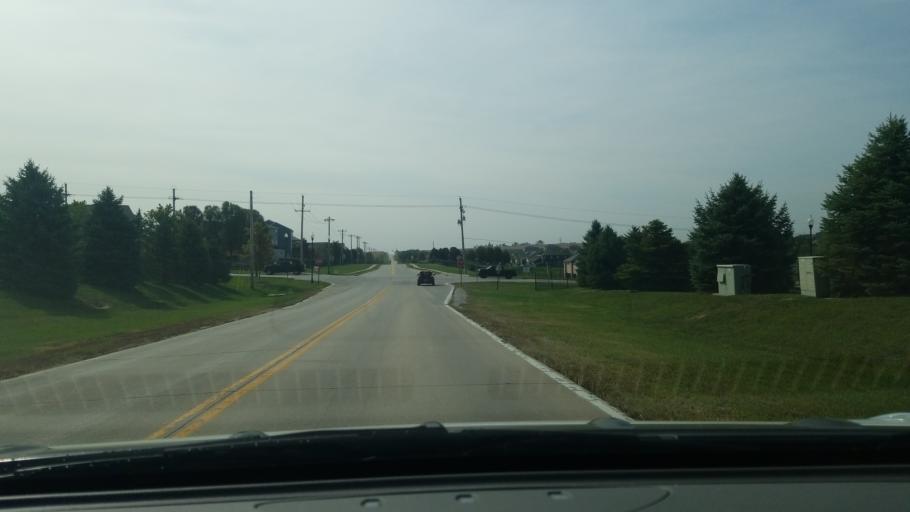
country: US
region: Nebraska
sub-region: Sarpy County
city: Papillion
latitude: 41.1337
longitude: -96.0622
